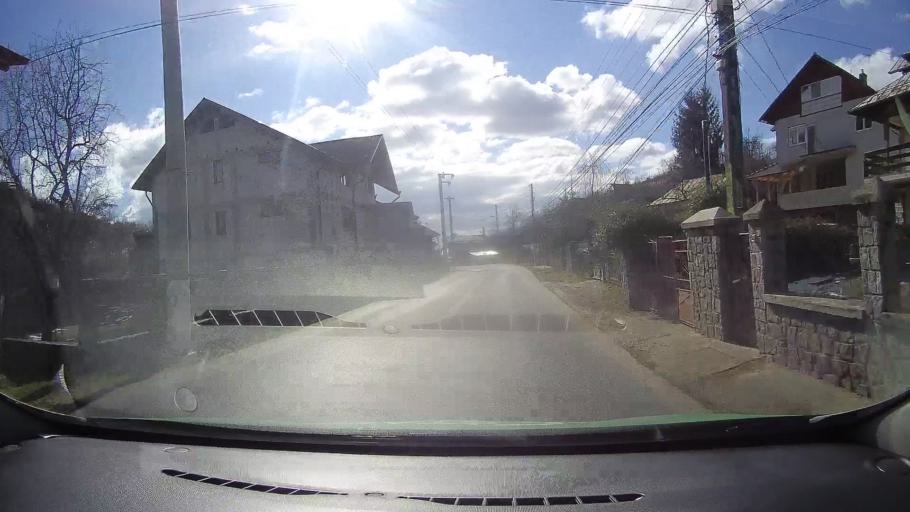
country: RO
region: Dambovita
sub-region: Comuna Runcu
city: Badeni
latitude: 45.1685
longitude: 25.3948
